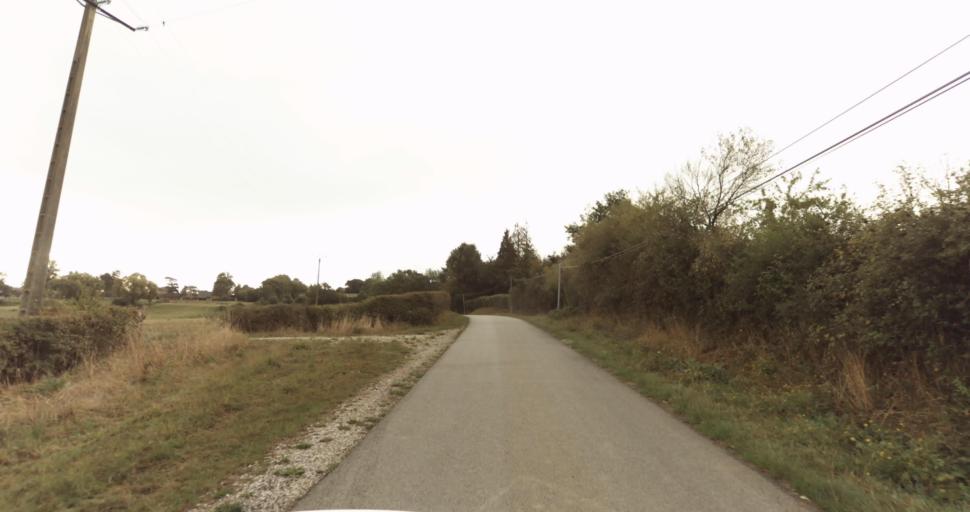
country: FR
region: Lower Normandy
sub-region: Departement de l'Orne
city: Trun
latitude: 48.9231
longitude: 0.0915
